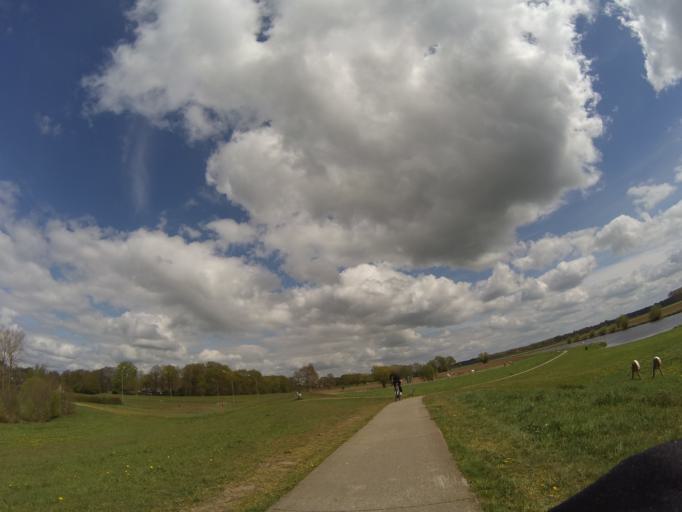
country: NL
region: Overijssel
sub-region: Gemeente Dalfsen
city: Dalfsen
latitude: 52.5041
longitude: 6.2670
